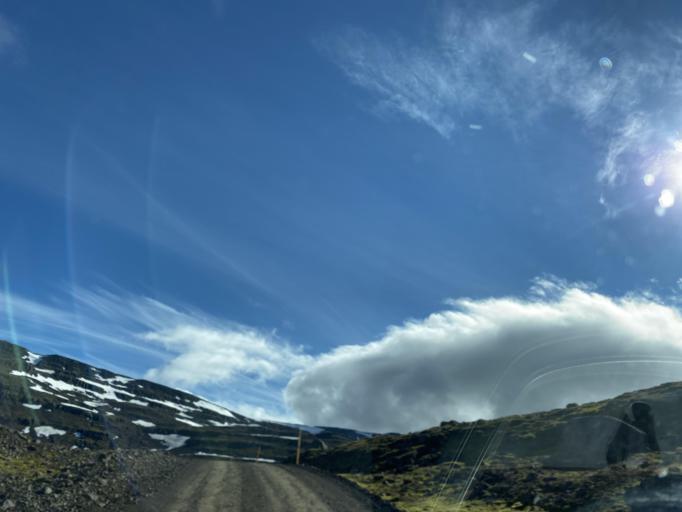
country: IS
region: East
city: Eskifjoerdur
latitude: 65.1721
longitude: -14.1196
